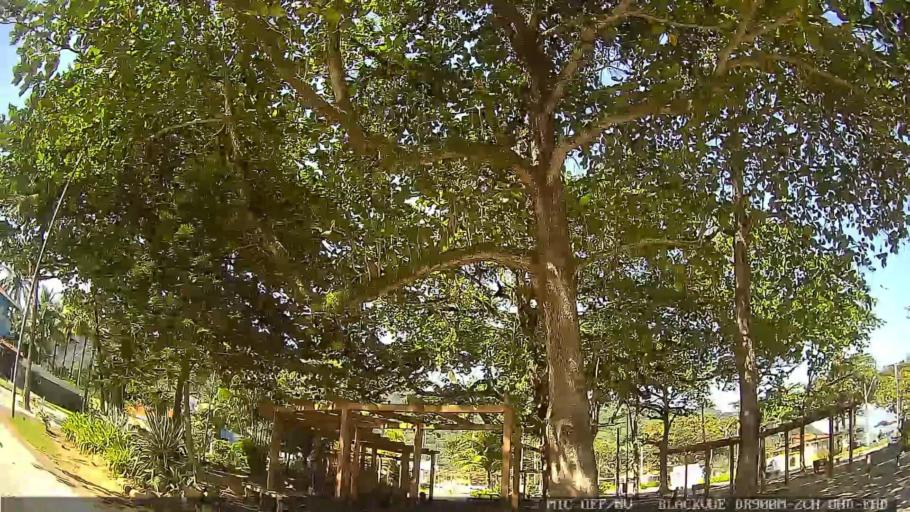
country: BR
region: Sao Paulo
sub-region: Guaruja
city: Guaruja
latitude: -24.0184
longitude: -46.2952
